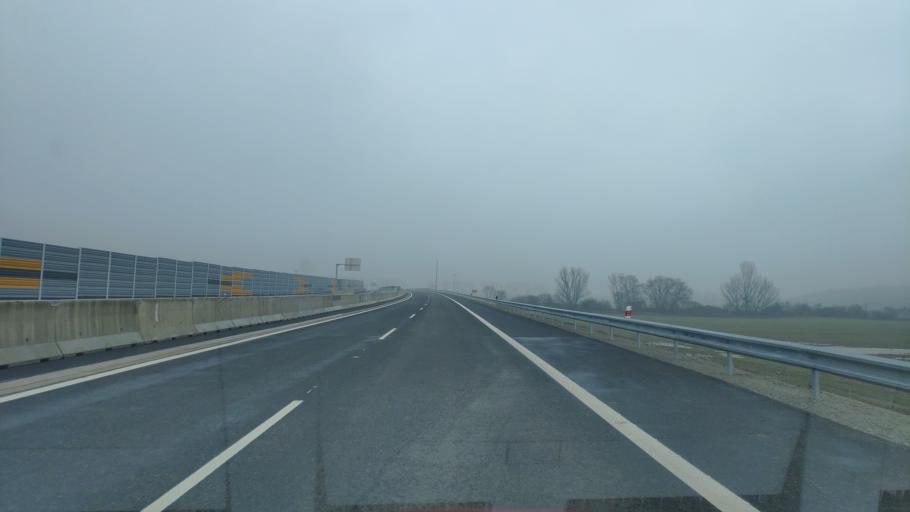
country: SK
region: Kosicky
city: Kosice
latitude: 48.7669
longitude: 21.3255
